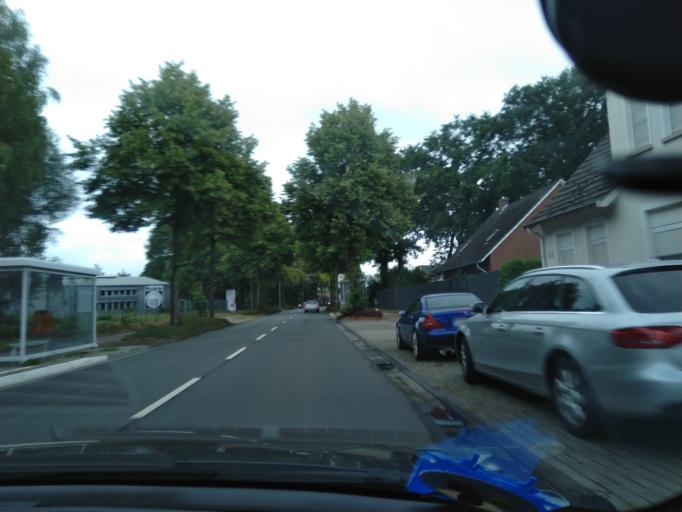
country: DE
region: Lower Saxony
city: Nordhorn
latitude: 52.4227
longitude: 7.0808
